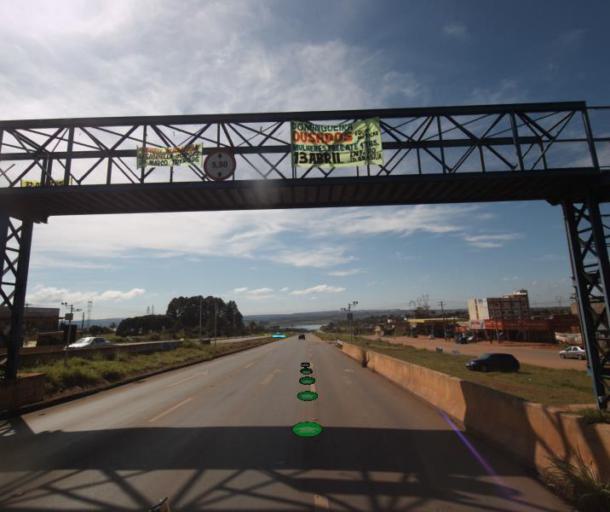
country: BR
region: Federal District
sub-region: Brasilia
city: Brasilia
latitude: -15.7600
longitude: -48.2461
